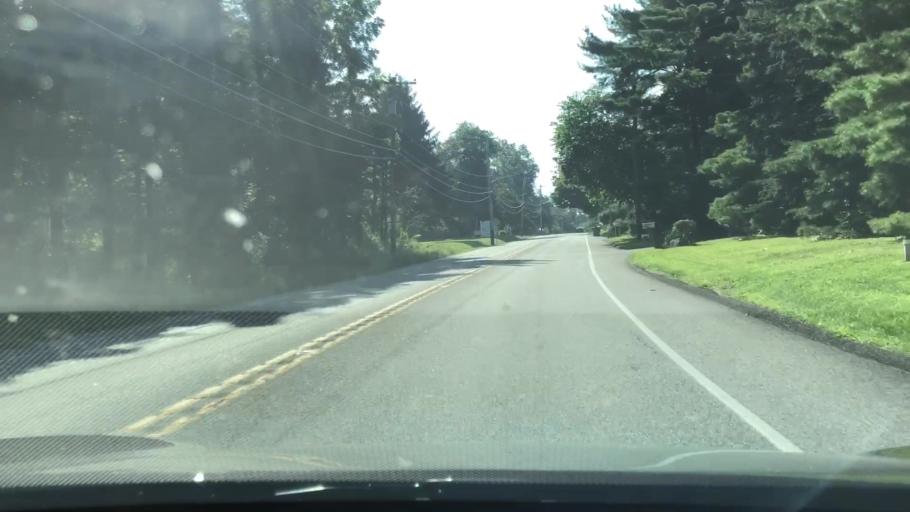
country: US
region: Pennsylvania
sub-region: Montgomery County
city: Dresher
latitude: 40.1542
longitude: -75.1739
